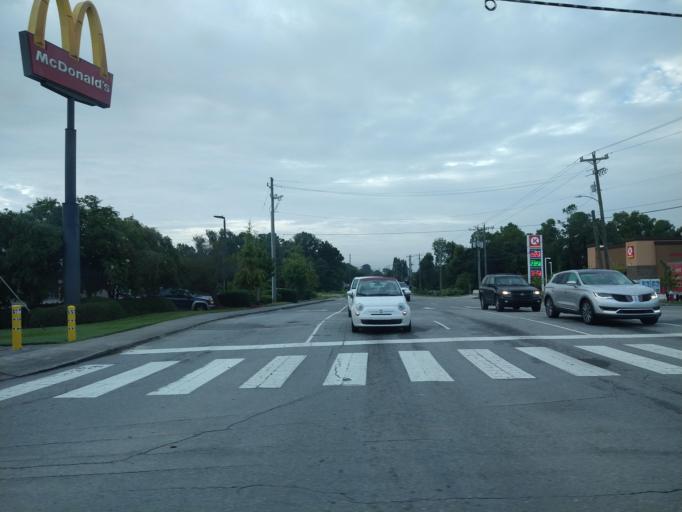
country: US
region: North Carolina
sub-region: Onslow County
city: Jacksonville
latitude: 34.7608
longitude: -77.4154
